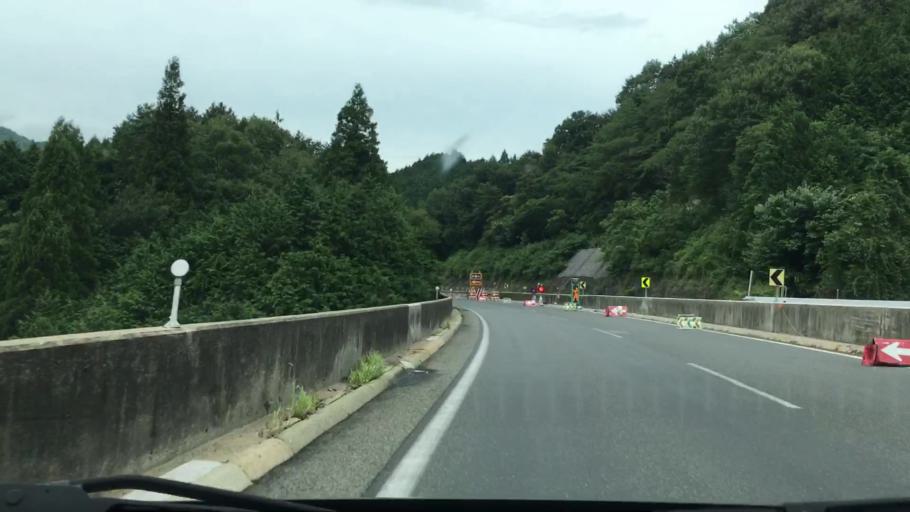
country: JP
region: Okayama
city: Niimi
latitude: 35.0179
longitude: 133.5836
